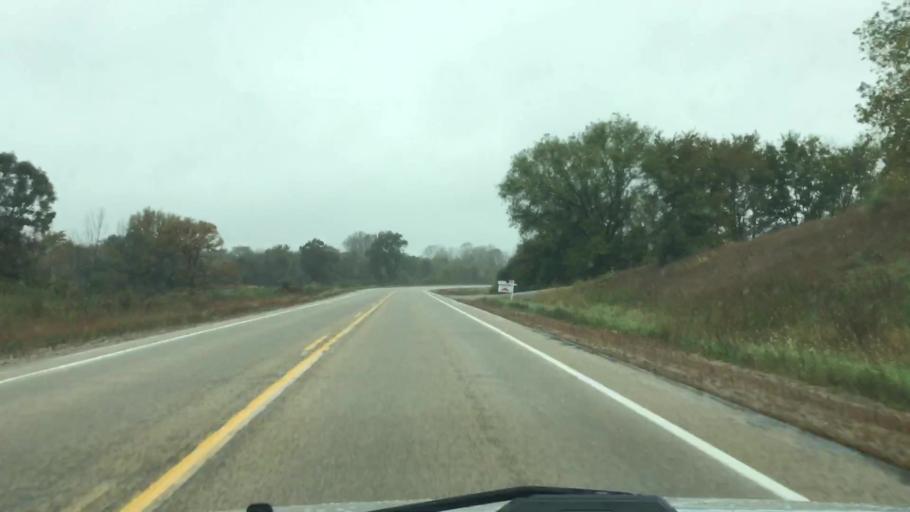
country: US
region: Wisconsin
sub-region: Jefferson County
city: Palmyra
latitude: 42.8799
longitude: -88.5479
